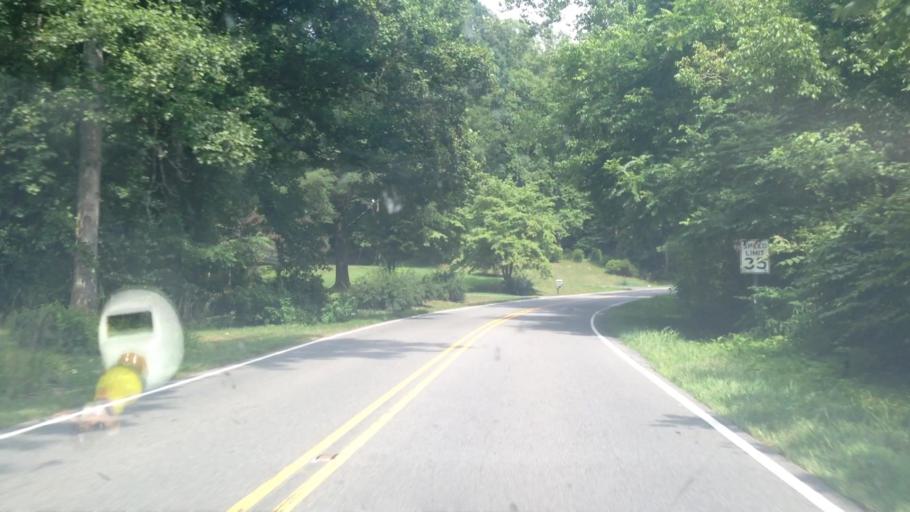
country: US
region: North Carolina
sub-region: Surry County
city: Mount Airy
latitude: 36.4815
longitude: -80.5821
